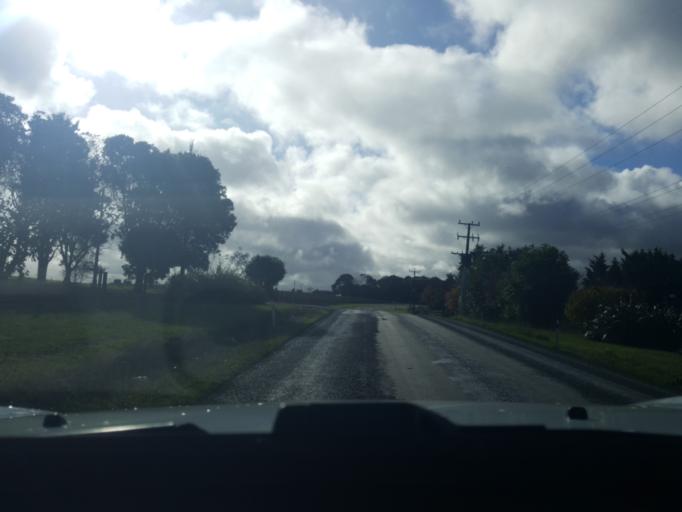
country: NZ
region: Auckland
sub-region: Auckland
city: Pukekohe East
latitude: -37.3023
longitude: 175.0192
